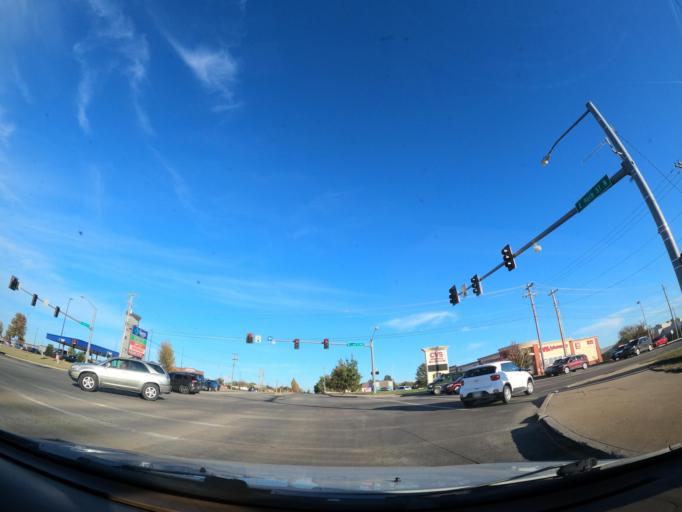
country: US
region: Oklahoma
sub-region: Tulsa County
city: Owasso
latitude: 36.2929
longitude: -95.8304
